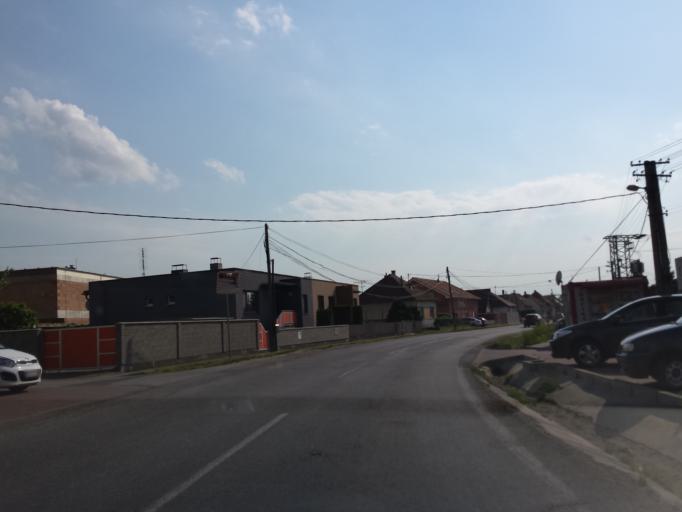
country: SK
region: Bratislavsky
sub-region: Okres Malacky
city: Malacky
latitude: 48.4450
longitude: 16.9849
